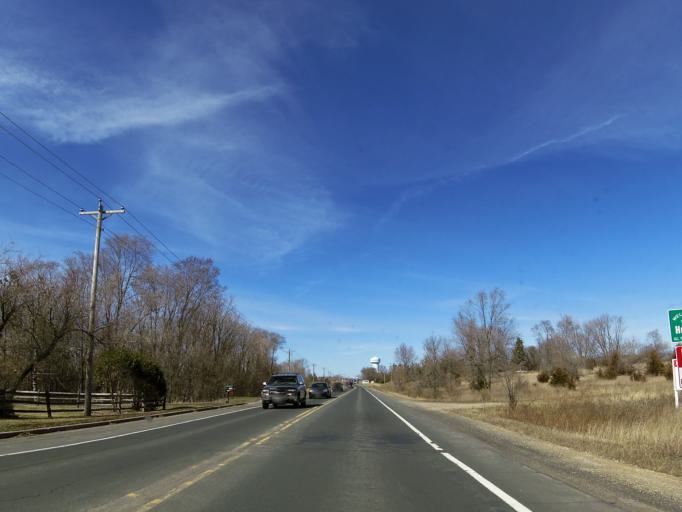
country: US
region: Wisconsin
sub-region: Saint Croix County
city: Hudson
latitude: 44.9714
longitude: -92.7210
